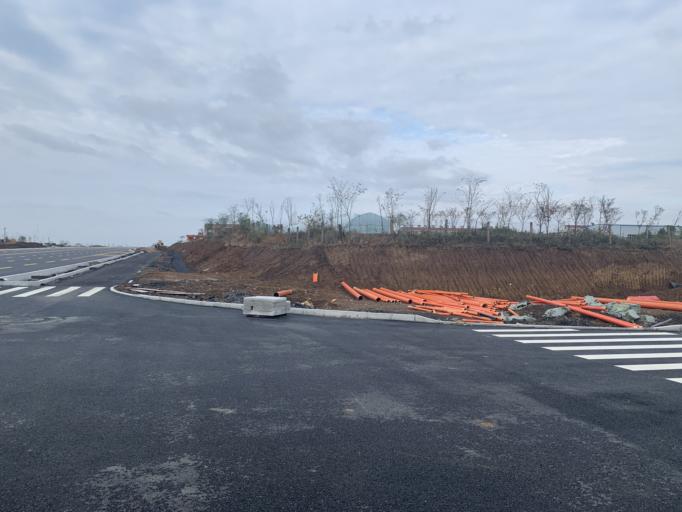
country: CN
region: Hubei
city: Anlu
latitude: 31.2498
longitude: 113.6522
